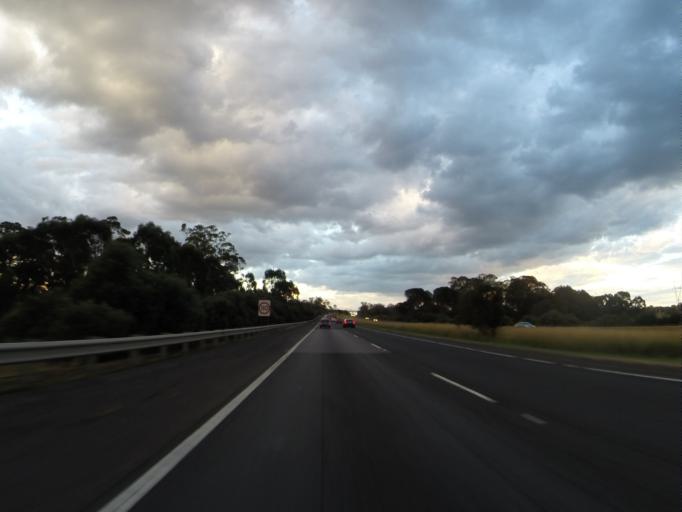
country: AU
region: New South Wales
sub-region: Campbelltown Municipality
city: Glen Alpine
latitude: -34.0963
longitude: 150.7649
